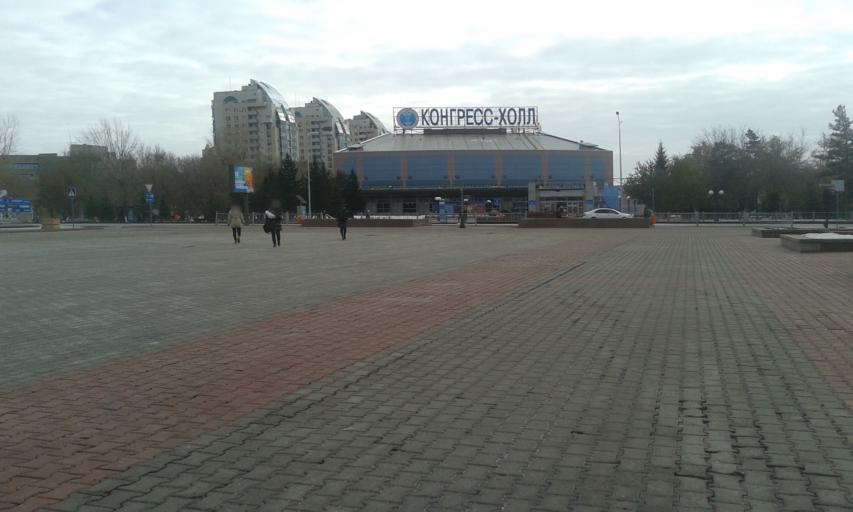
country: KZ
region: Astana Qalasy
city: Astana
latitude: 51.1653
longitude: 71.4209
